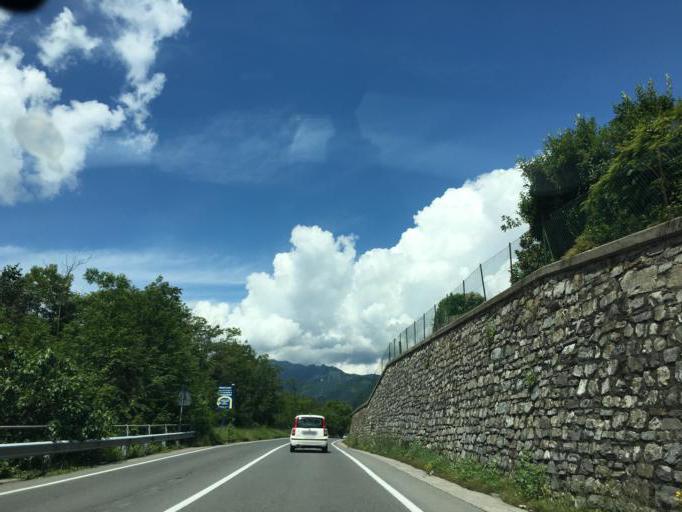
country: IT
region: Lombardy
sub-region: Provincia di Como
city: Codogna-Cardano
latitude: 46.0290
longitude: 9.1985
